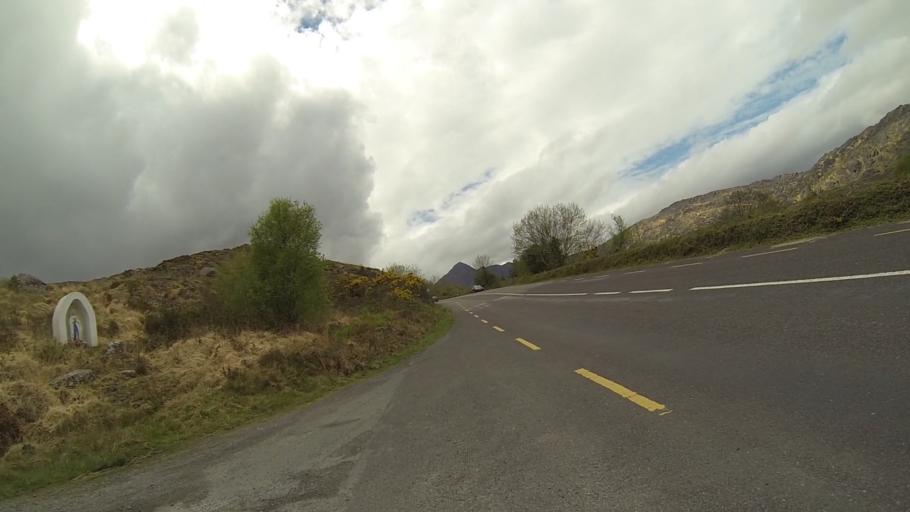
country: IE
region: Munster
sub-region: County Cork
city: Bantry
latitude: 51.7276
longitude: -9.5702
